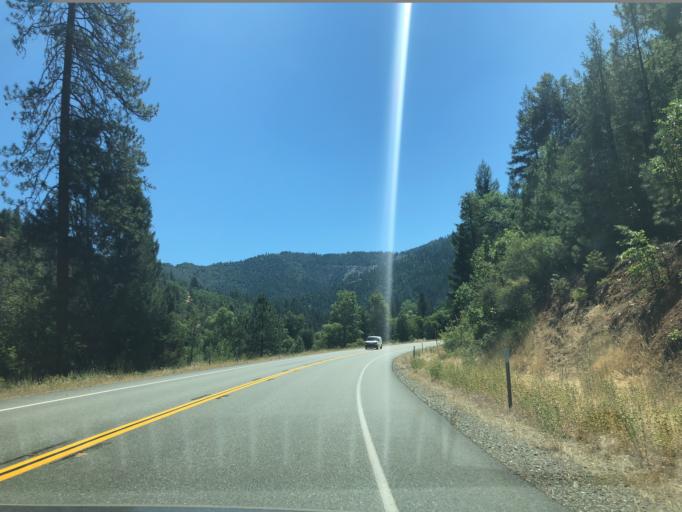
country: US
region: California
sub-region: Trinity County
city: Weaverville
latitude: 40.6583
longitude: -122.9168
